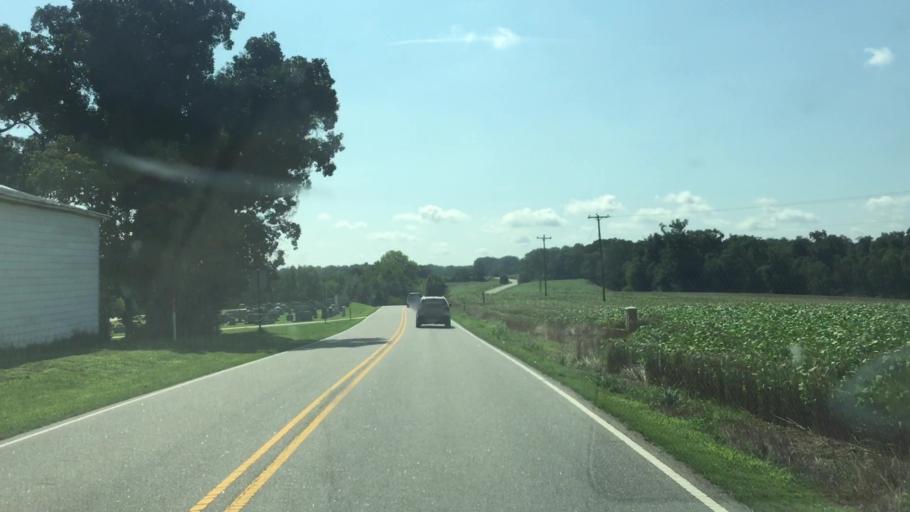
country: US
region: North Carolina
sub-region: Anson County
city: Burnsville
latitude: 35.1035
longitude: -80.3188
